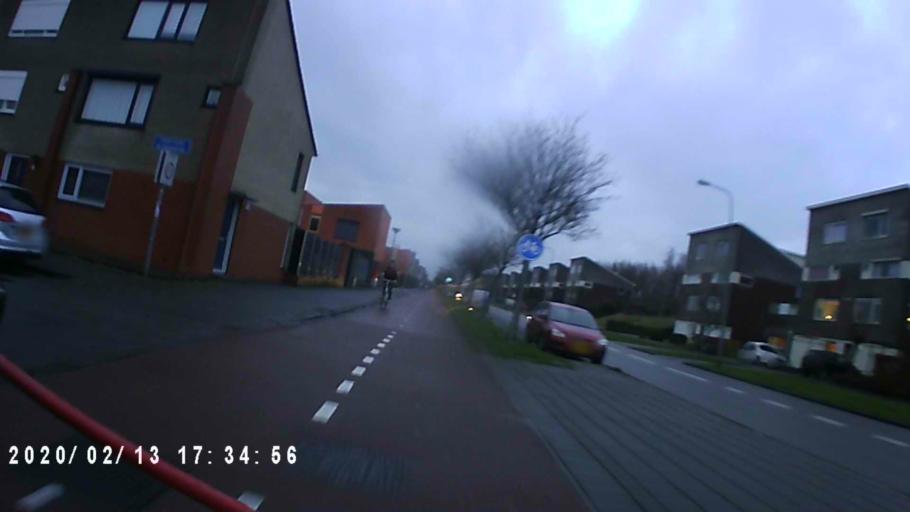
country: NL
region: Groningen
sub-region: Gemeente Groningen
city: Groningen
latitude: 53.2229
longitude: 6.5134
